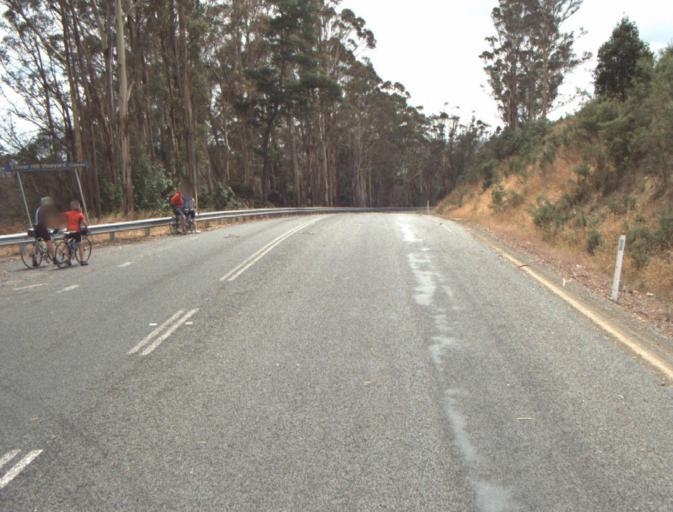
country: AU
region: Tasmania
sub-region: Dorset
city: Bridport
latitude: -41.1692
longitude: 147.2308
